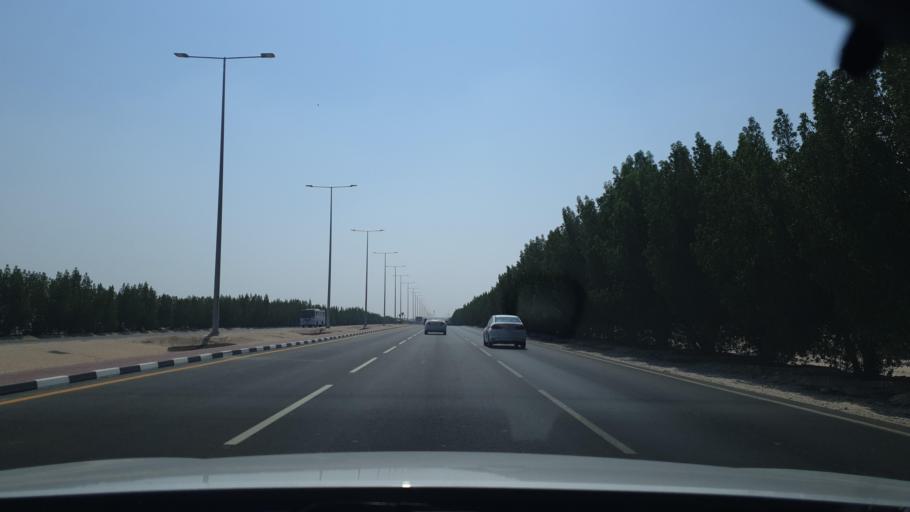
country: QA
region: Al Khawr
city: Al Khawr
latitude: 25.7050
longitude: 51.5042
